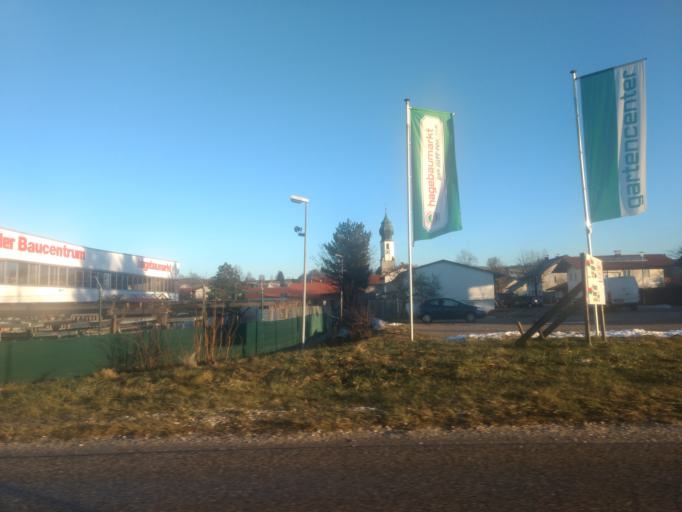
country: DE
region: Bavaria
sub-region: Upper Bavaria
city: Nussdorf
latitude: 47.8747
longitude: 12.5867
